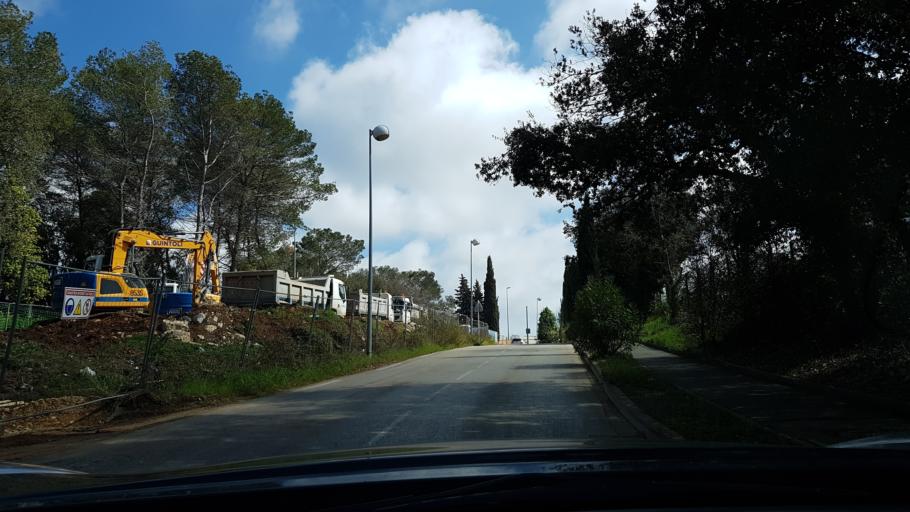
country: FR
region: Provence-Alpes-Cote d'Azur
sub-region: Departement des Alpes-Maritimes
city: Biot
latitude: 43.6081
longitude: 7.0746
